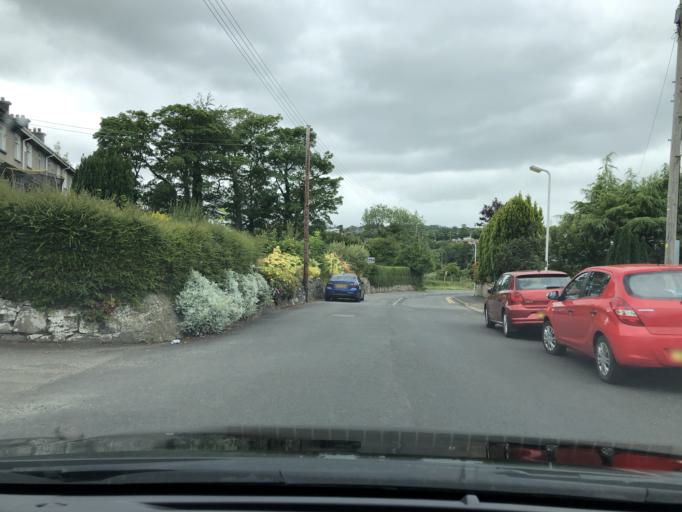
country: GB
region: Northern Ireland
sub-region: Larne District
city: Larne
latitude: 54.8486
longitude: -5.8317
